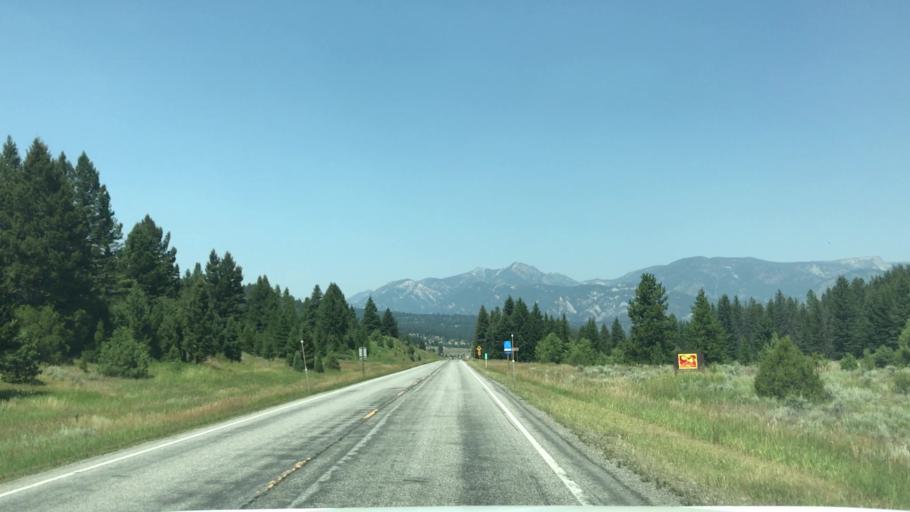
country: US
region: Montana
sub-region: Gallatin County
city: Big Sky
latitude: 45.2080
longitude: -111.2444
